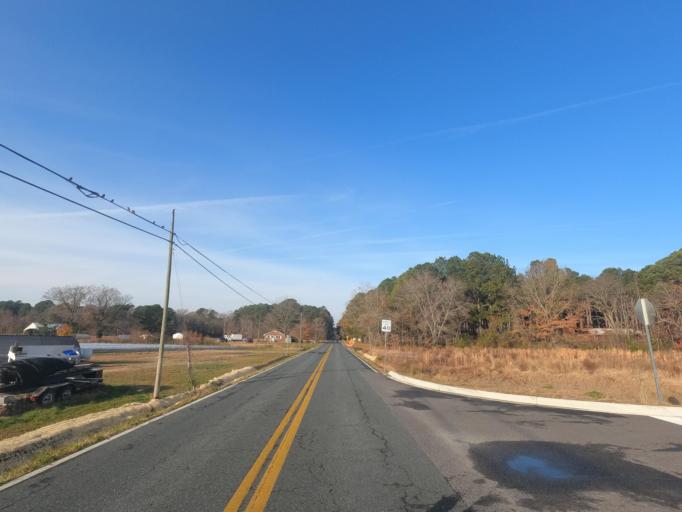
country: US
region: Maryland
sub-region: Somerset County
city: Crisfield
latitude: 38.0333
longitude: -75.7818
